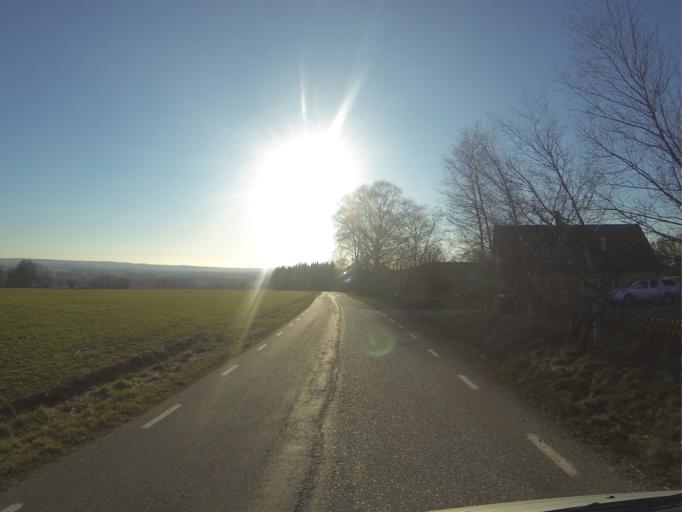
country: SE
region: Skane
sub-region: Hoors Kommun
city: Loberod
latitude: 55.7476
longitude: 13.4449
